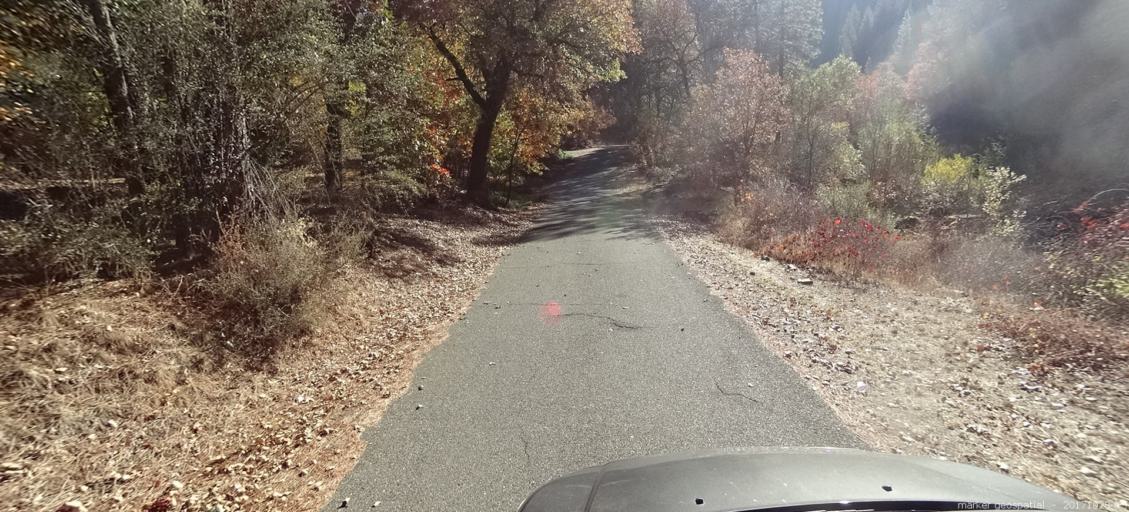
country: US
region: California
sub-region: Shasta County
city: Shasta
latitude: 40.7591
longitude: -122.5791
